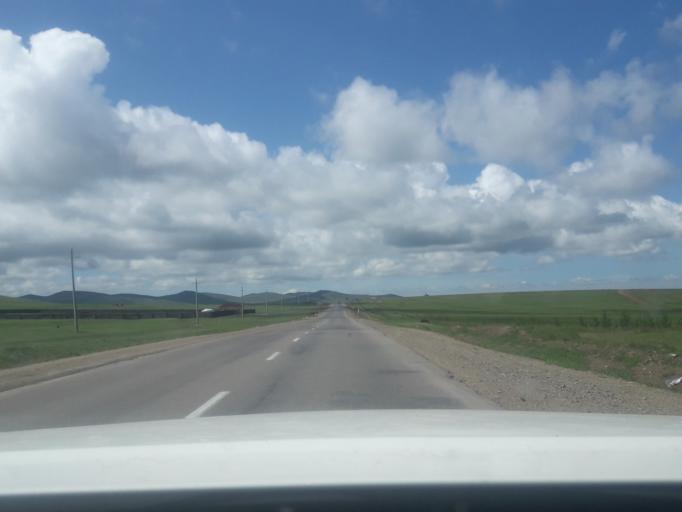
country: MN
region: Central Aimak
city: Altanbulag
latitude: 47.9012
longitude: 106.4893
